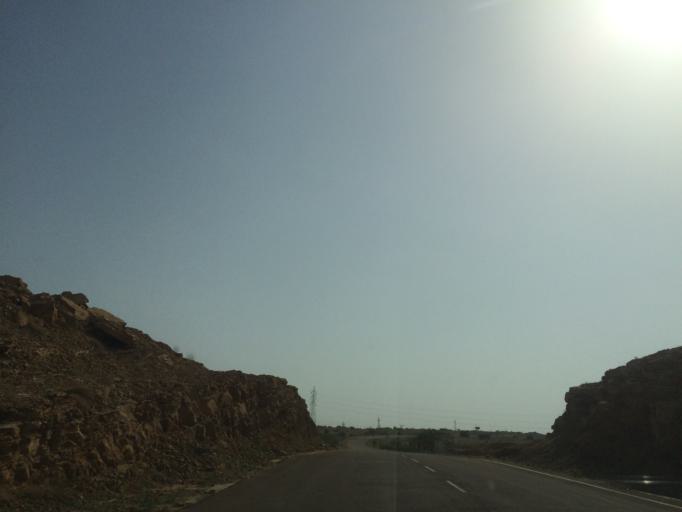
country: IN
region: Rajasthan
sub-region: Jaisalmer
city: Jaisalmer
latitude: 26.9182
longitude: 70.8054
